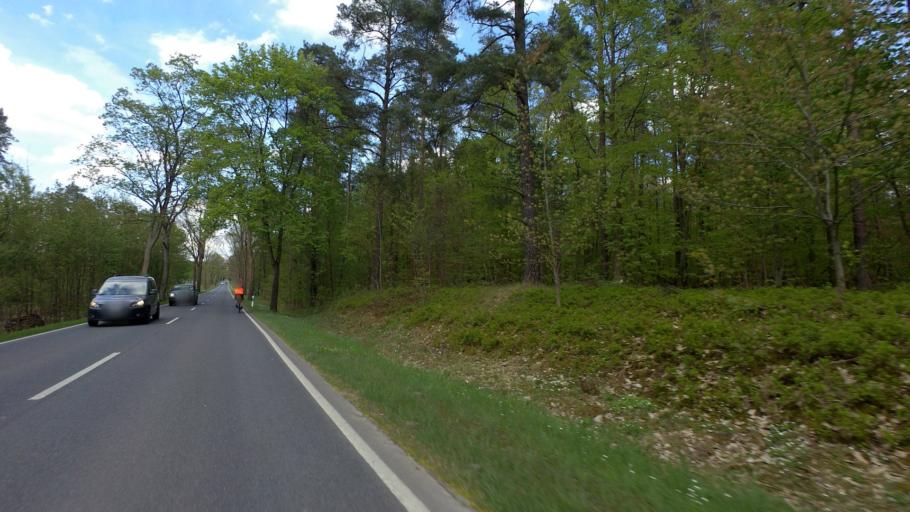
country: DE
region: Brandenburg
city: Friedrichswalde
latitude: 52.9774
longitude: 13.5806
